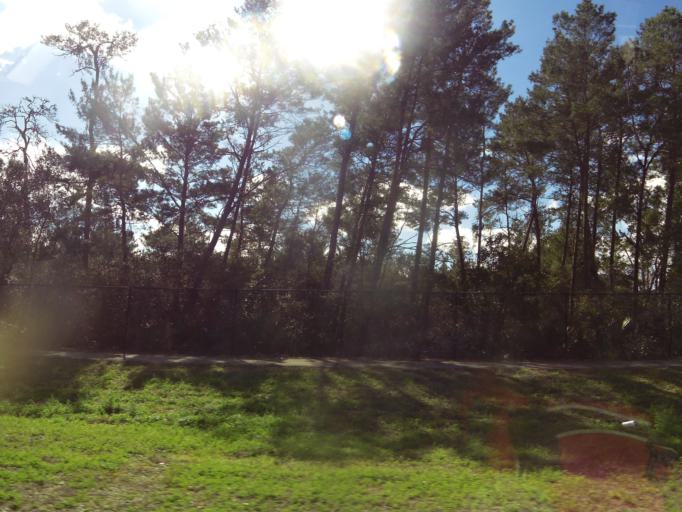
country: US
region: Florida
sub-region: Volusia County
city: Orange City
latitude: 28.9341
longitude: -81.3089
